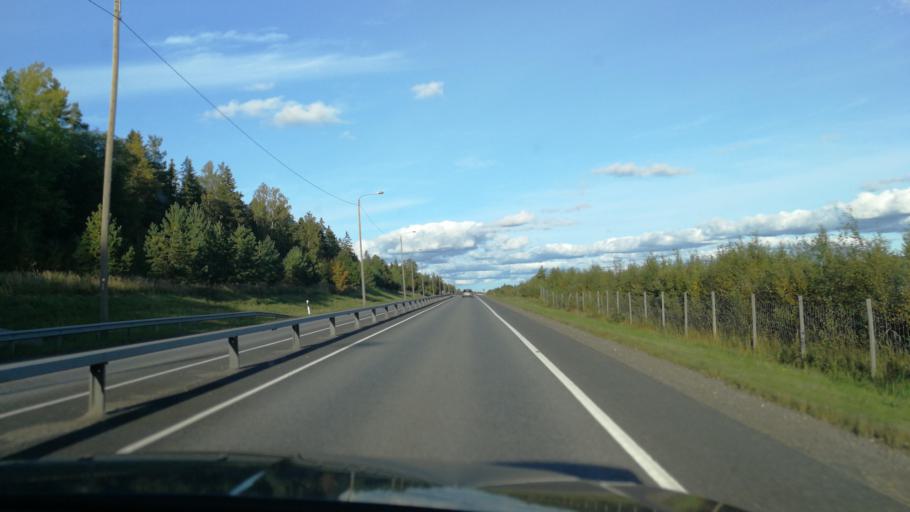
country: FI
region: Satakunta
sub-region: Rauma
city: Rauma
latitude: 61.1595
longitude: 21.5892
